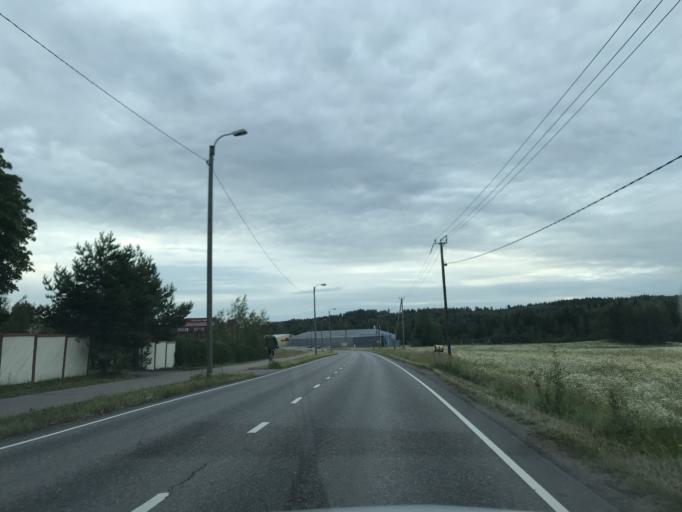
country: FI
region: Uusimaa
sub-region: Helsinki
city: Nurmijaervi
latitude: 60.3812
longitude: 24.7328
